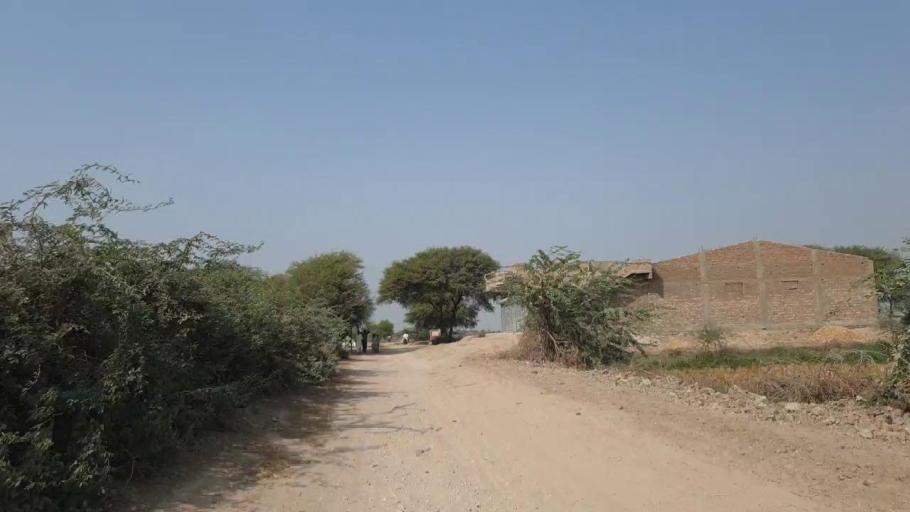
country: PK
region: Sindh
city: Kario
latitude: 24.9312
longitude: 68.5592
